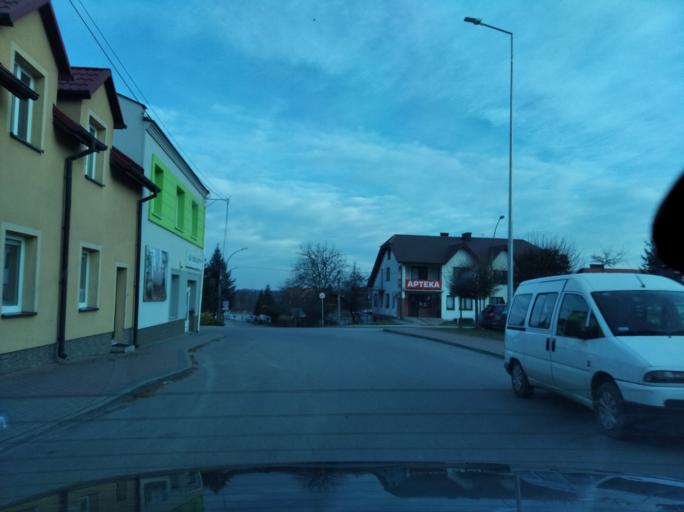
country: PL
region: Subcarpathian Voivodeship
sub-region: Powiat ropczycko-sedziszowski
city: Sedziszow Malopolski
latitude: 50.0716
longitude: 21.7019
